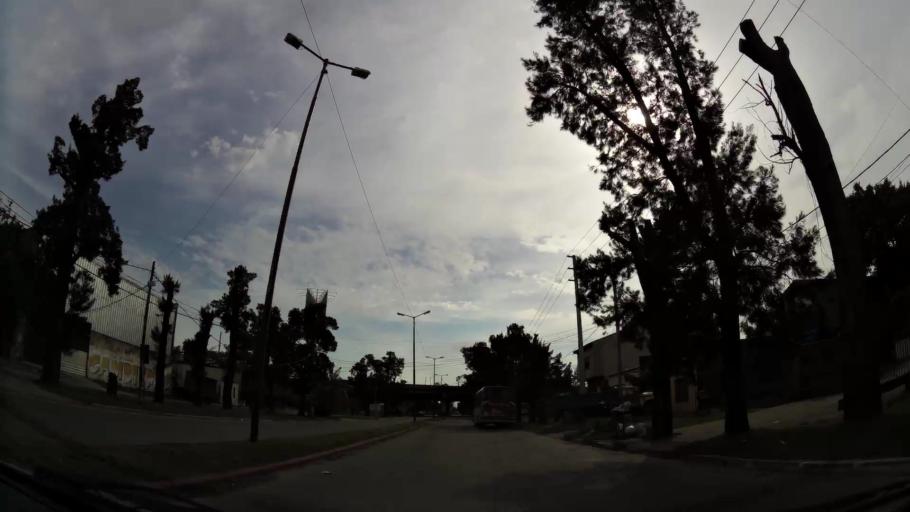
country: AR
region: Buenos Aires
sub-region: Partido de Quilmes
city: Quilmes
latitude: -34.7154
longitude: -58.2451
